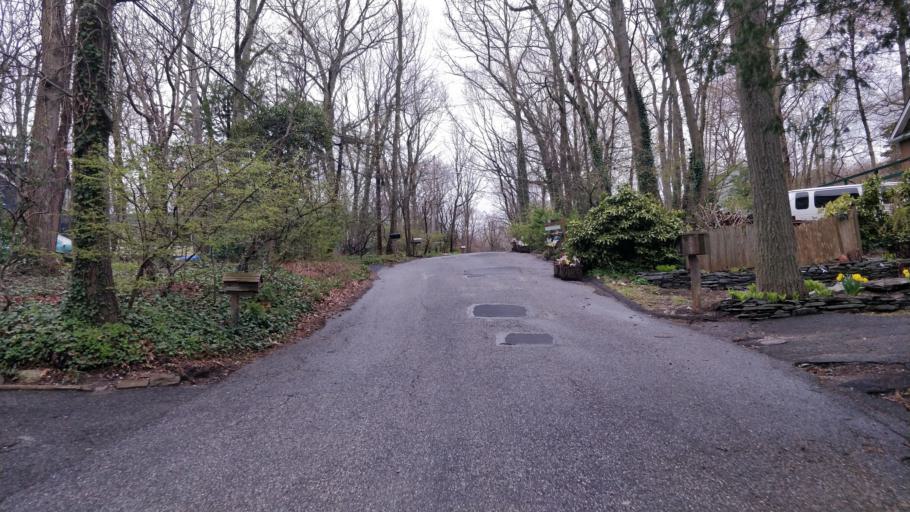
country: US
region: New York
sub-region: Suffolk County
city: Port Jefferson
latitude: 40.9521
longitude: -73.0847
